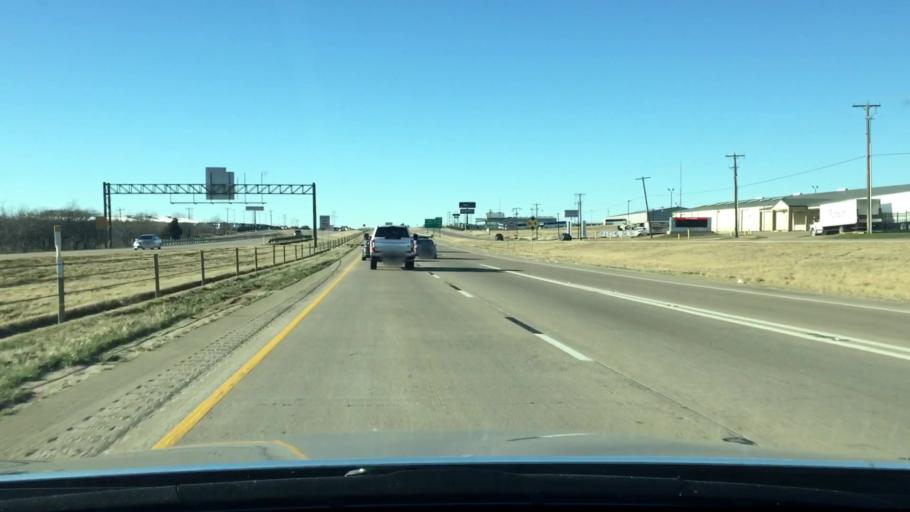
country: US
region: Texas
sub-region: Johnson County
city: Alvarado
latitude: 32.4239
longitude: -97.2313
